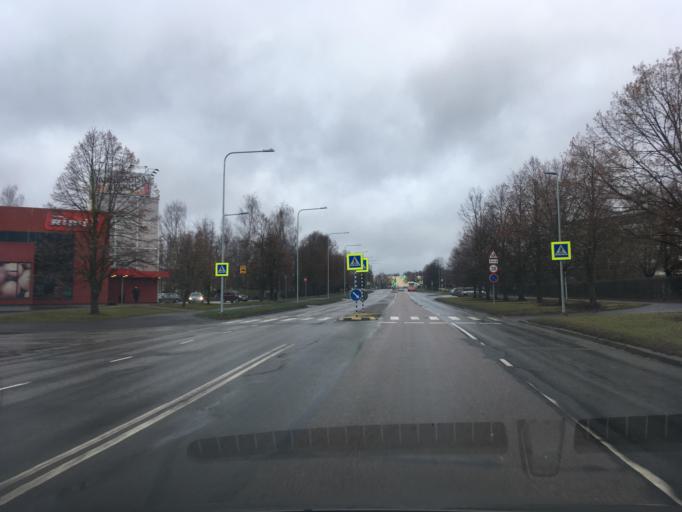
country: EE
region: Tartu
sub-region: Tartu linn
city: Tartu
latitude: 58.3735
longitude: 26.7681
